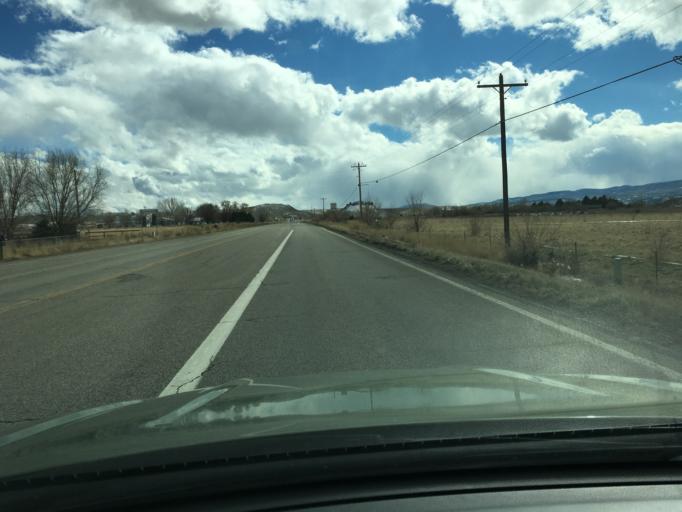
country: US
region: Colorado
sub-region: Mesa County
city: Clifton
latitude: 39.0335
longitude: -108.4596
